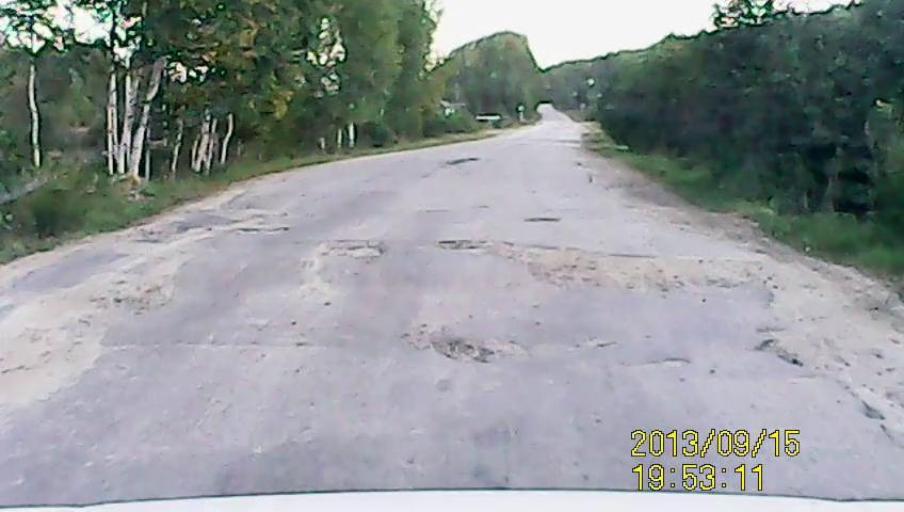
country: RU
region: Chelyabinsk
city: Kyshtym
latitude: 55.7649
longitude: 60.4857
